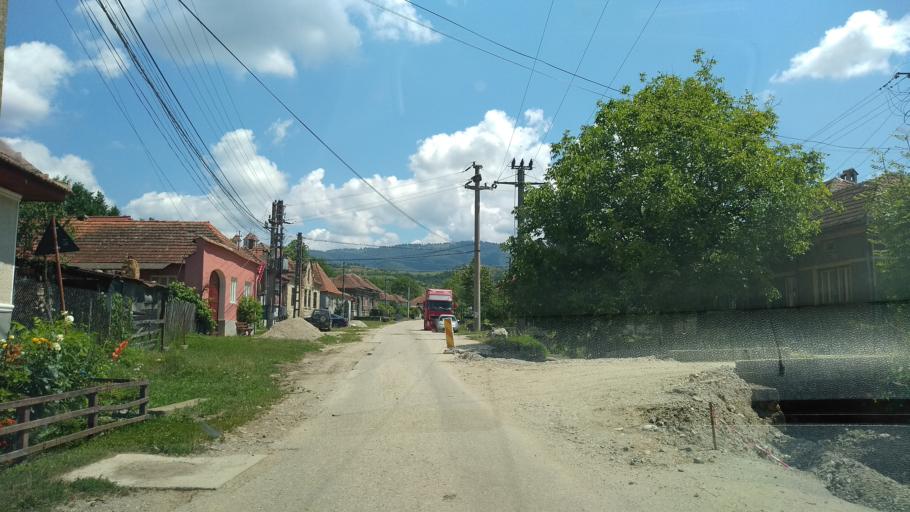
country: RO
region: Hunedoara
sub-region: Comuna Orastioara de Sus
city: Orastioara de Sus
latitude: 45.7107
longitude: 23.1269
